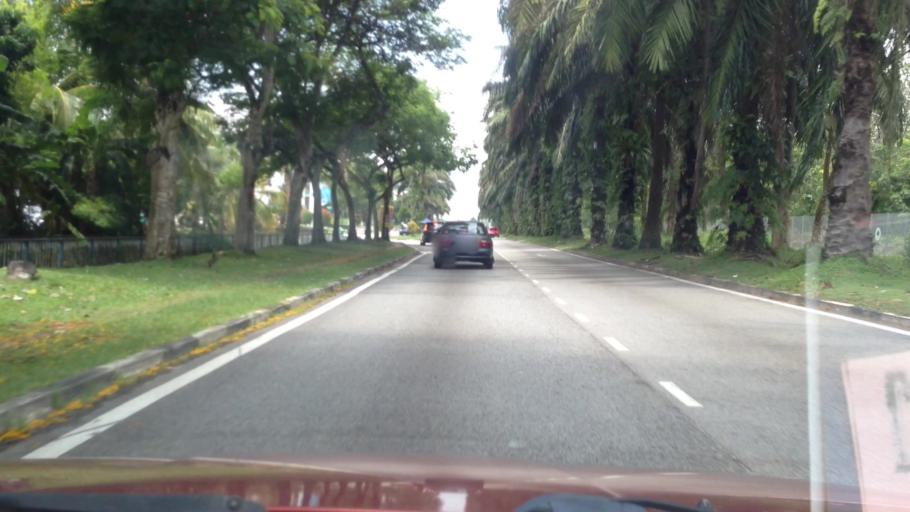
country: MY
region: Selangor
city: Kampung Baru Subang
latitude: 3.1733
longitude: 101.5498
